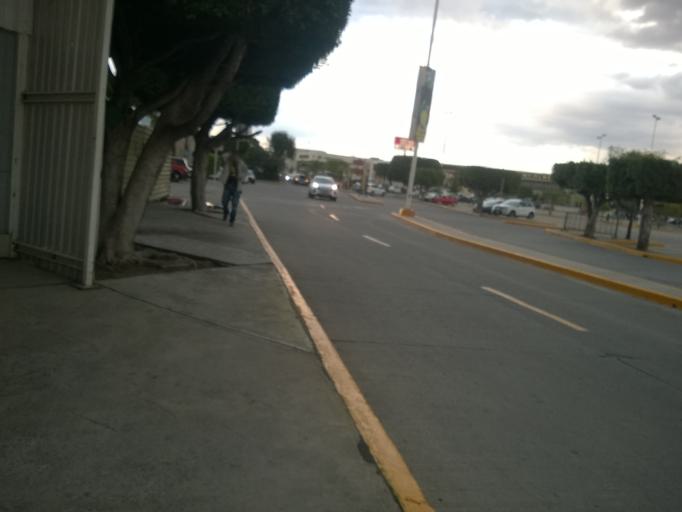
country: MX
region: Guanajuato
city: Leon
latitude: 21.1597
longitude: -101.6939
